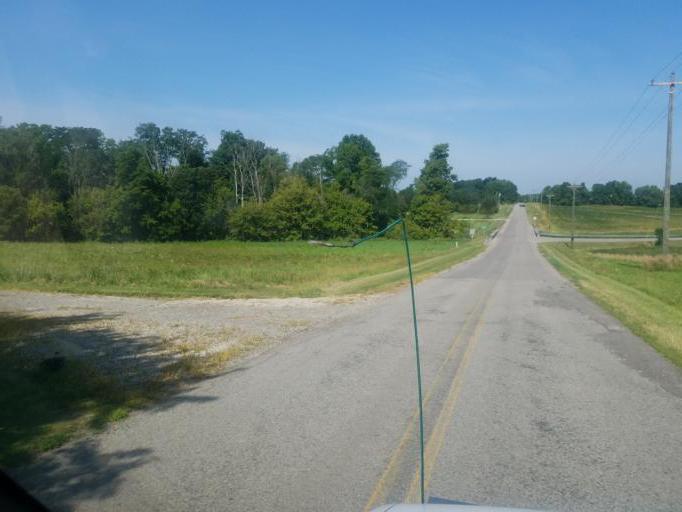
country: US
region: Ohio
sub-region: Union County
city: Marysville
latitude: 40.2836
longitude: -83.2807
